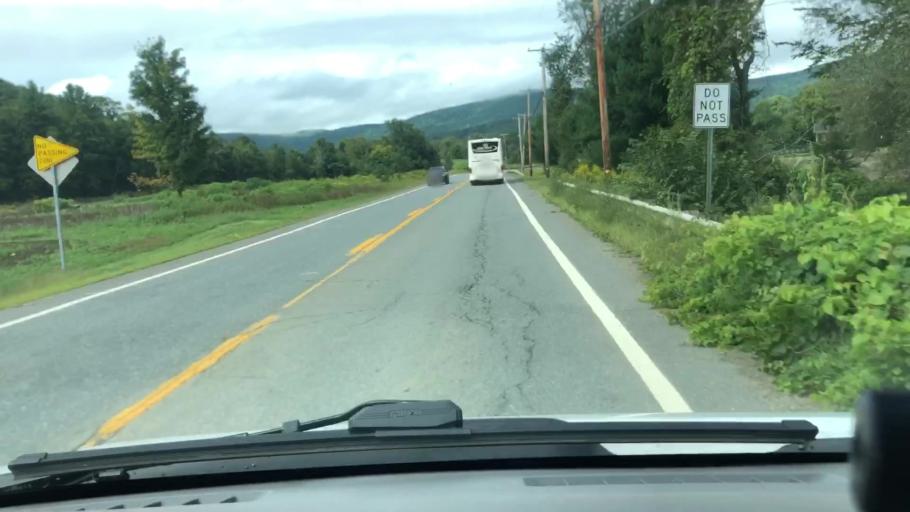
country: US
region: Massachusetts
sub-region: Franklin County
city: Buckland
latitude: 42.6069
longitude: -72.7750
